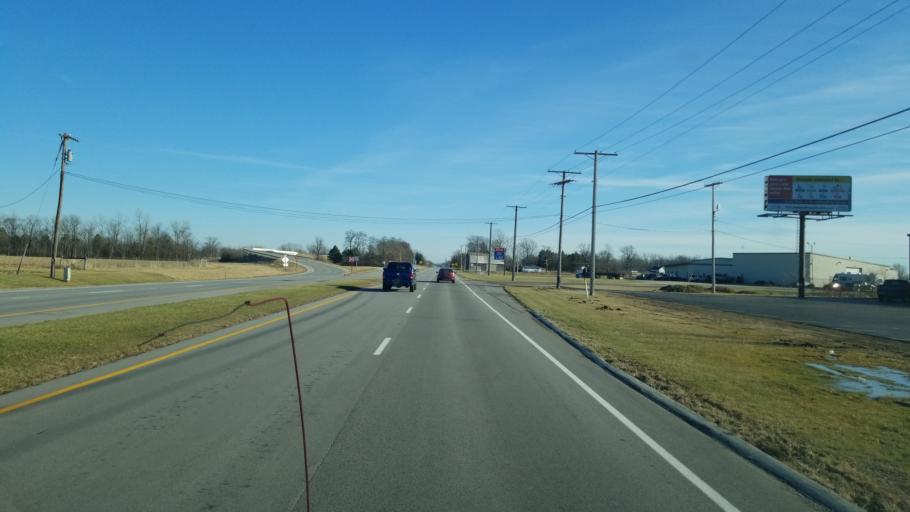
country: US
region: Ohio
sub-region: Sandusky County
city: Fremont
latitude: 41.3351
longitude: -83.0680
